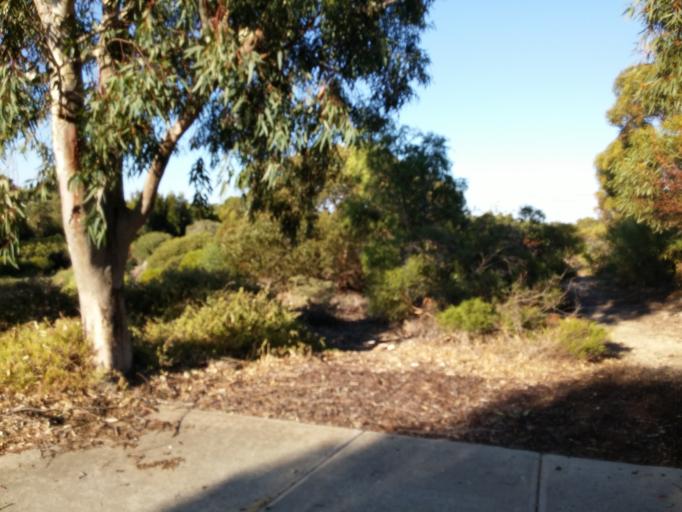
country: AU
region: Western Australia
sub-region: Fremantle
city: White Gum Valley
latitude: -32.0571
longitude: 115.7680
